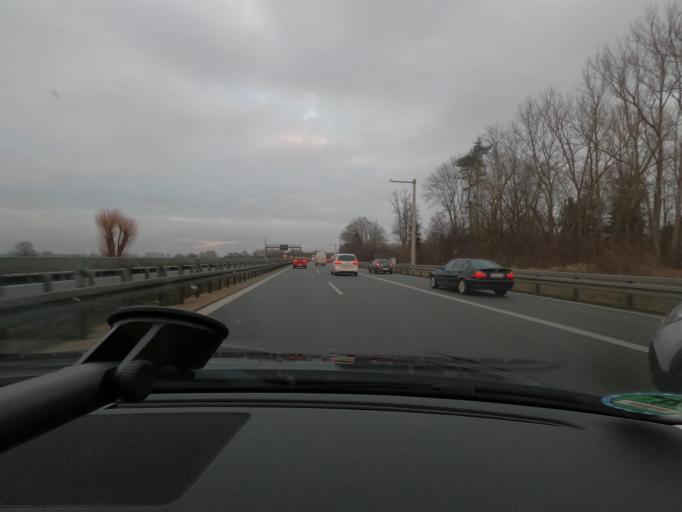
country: DE
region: Bavaria
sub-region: Regierungsbezirk Mittelfranken
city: Baiersdorf
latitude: 49.6464
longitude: 11.0217
